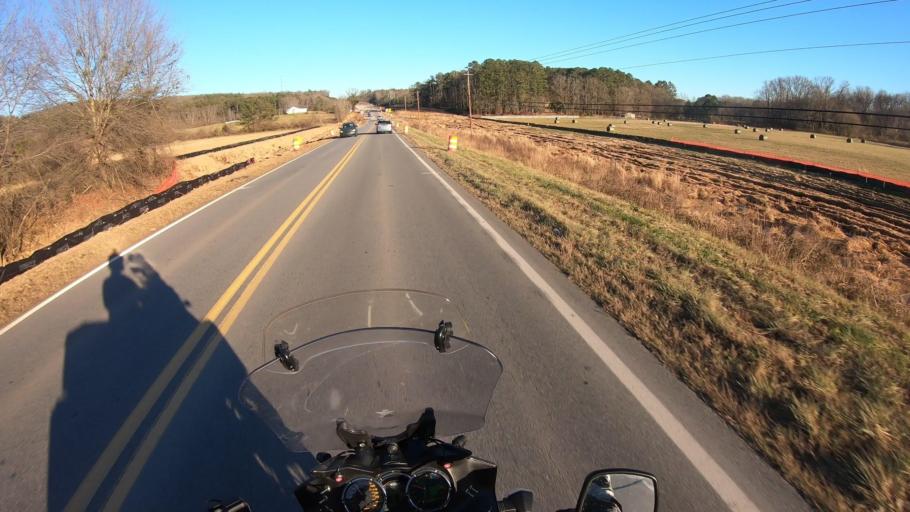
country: US
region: Georgia
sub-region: Bartow County
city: Emerson
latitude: 34.1154
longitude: -84.7865
